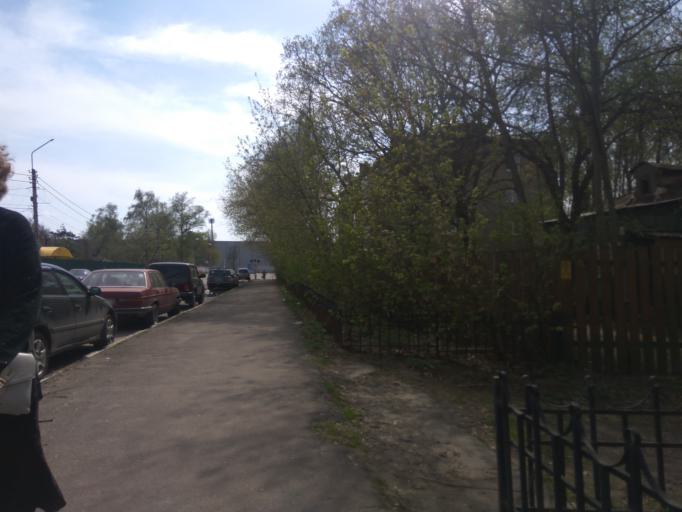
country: RU
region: Moskovskaya
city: Bykovo
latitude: 55.6235
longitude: 38.0671
